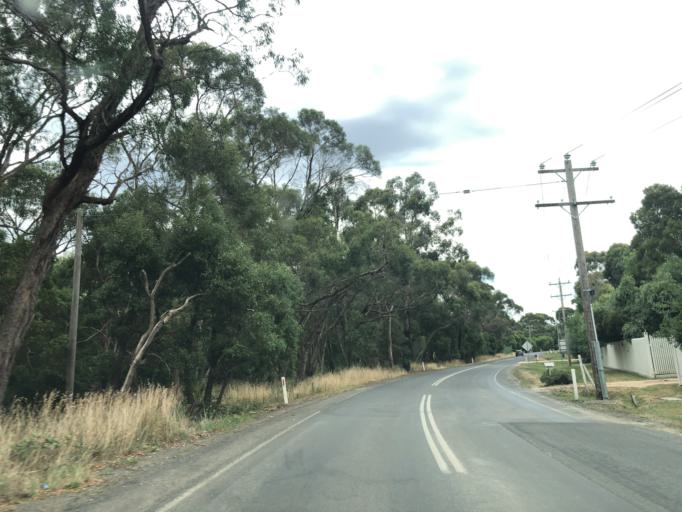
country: AU
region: Victoria
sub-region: Hume
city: Sunbury
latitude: -37.3650
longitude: 144.5158
